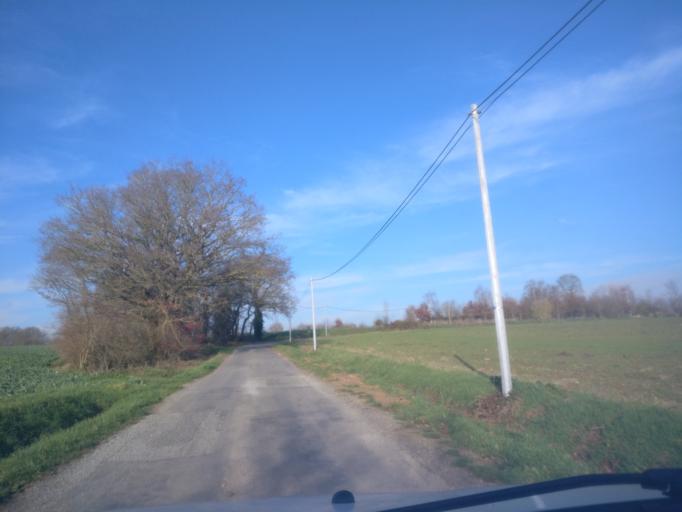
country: FR
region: Brittany
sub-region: Departement d'Ille-et-Vilaine
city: Livre-sur-Changeon
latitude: 48.2247
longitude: -1.3734
